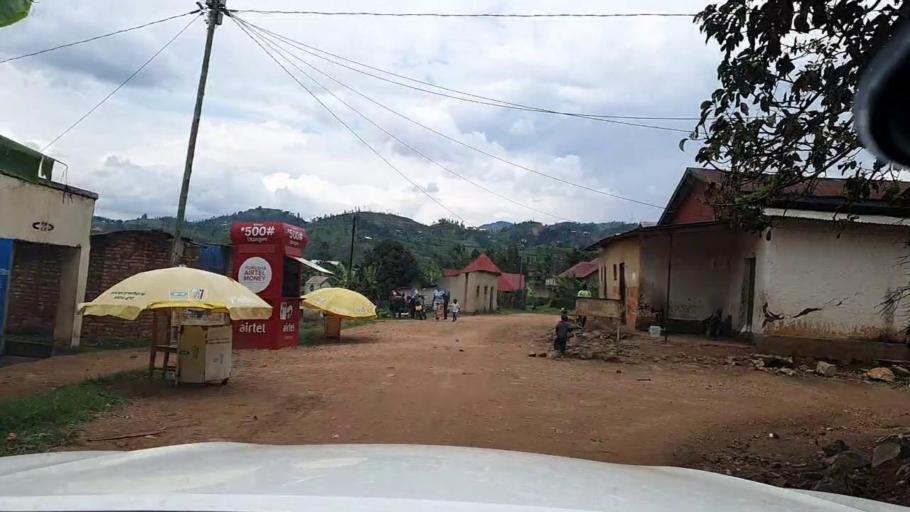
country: RW
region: Western Province
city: Kibuye
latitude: -2.0716
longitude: 29.4289
